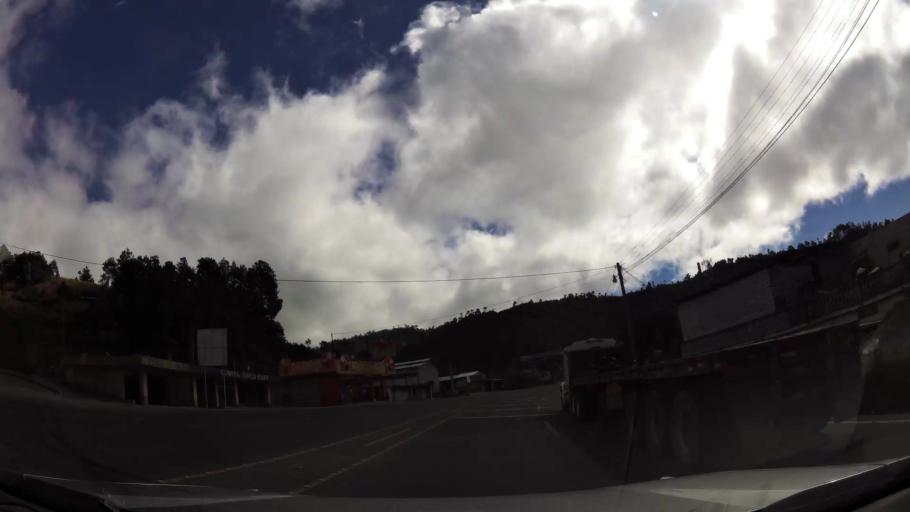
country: GT
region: Solola
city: Concepcion
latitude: 14.8431
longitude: -91.1744
